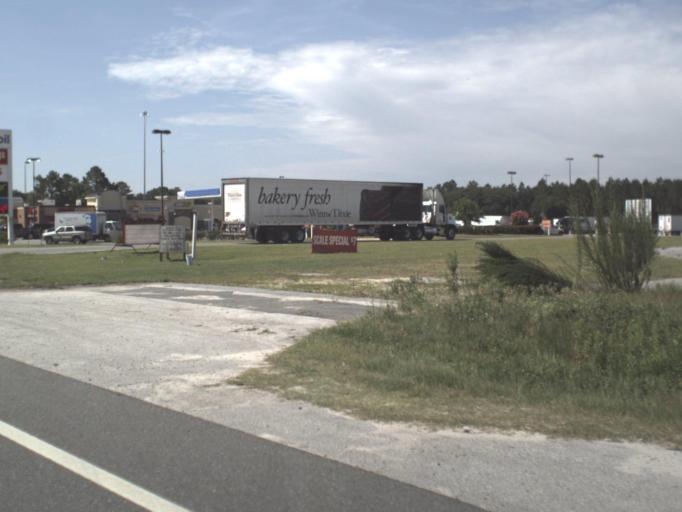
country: US
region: Florida
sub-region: Madison County
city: Madison
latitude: 30.3991
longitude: -83.3591
